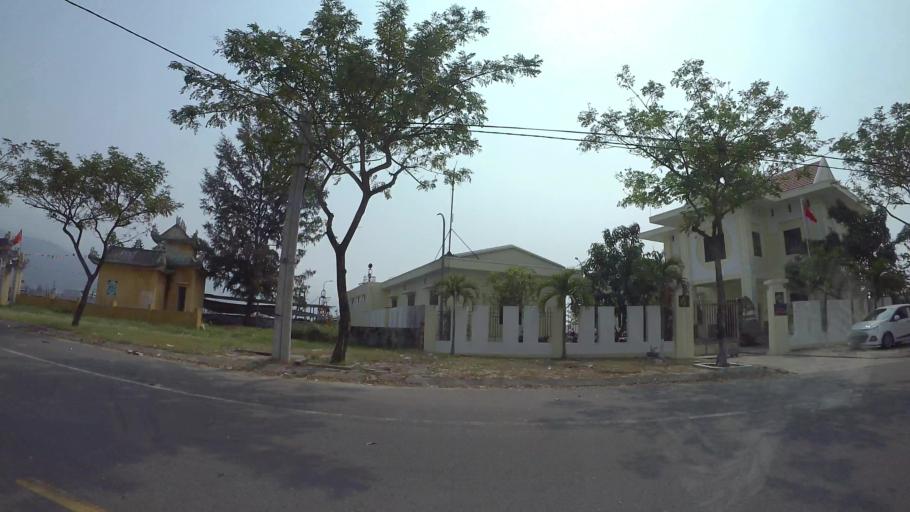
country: VN
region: Da Nang
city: Da Nang
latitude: 16.0997
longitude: 108.2348
